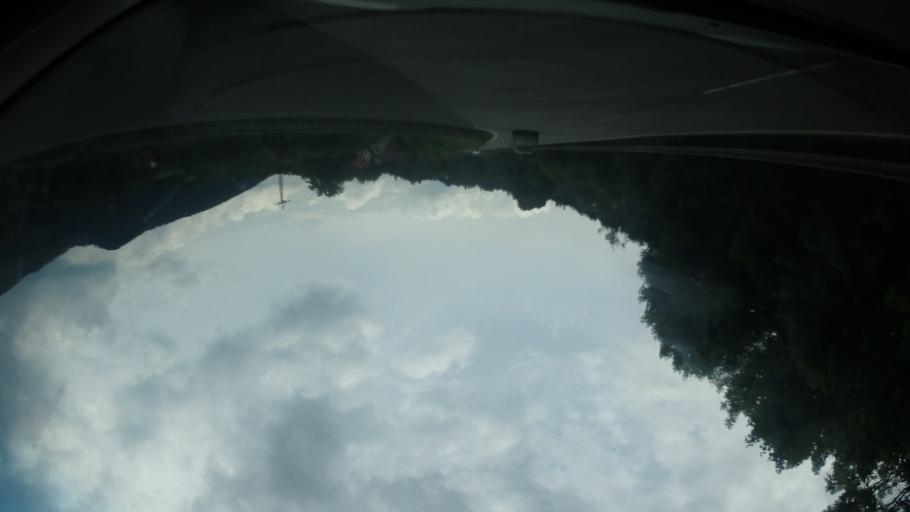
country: CZ
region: South Moravian
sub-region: Okres Brno-Venkov
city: Nedvedice
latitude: 49.5024
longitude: 16.3332
